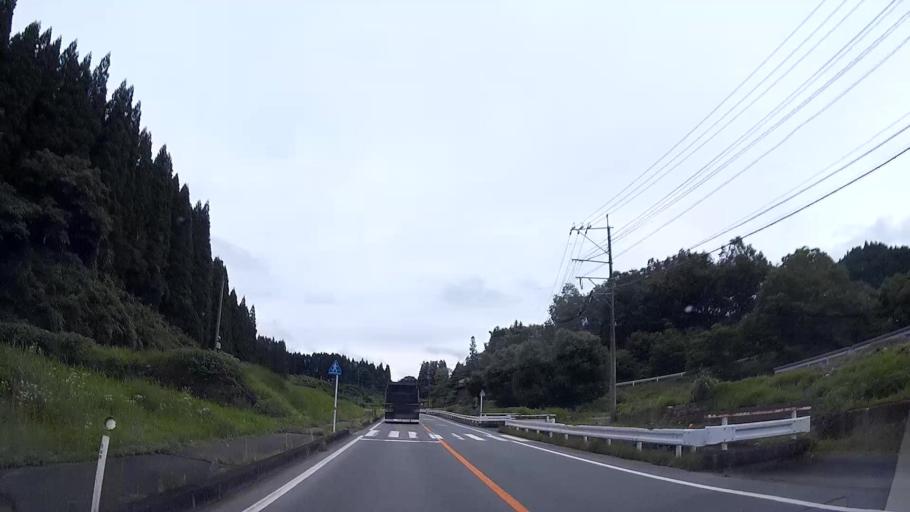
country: JP
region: Oita
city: Tsukawaki
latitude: 33.1246
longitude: 131.0403
